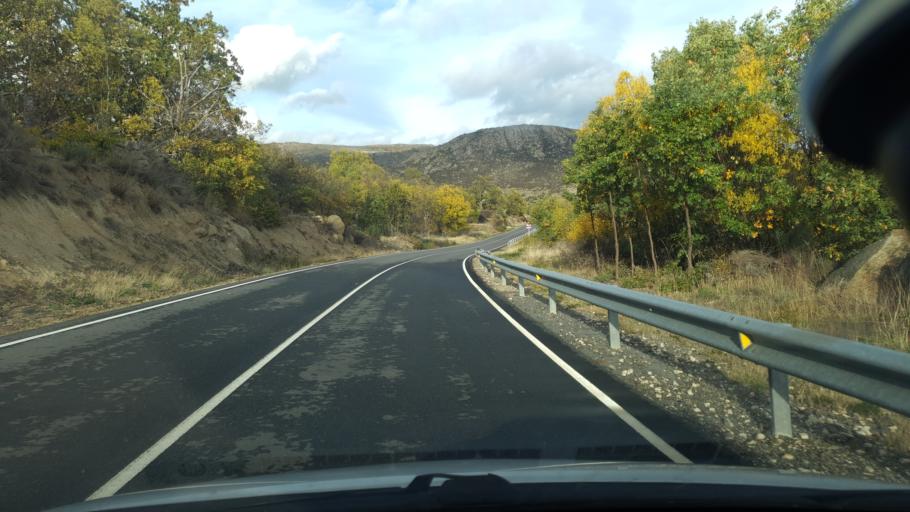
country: ES
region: Castille and Leon
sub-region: Provincia de Avila
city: Navaquesera
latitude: 40.4020
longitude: -4.9051
